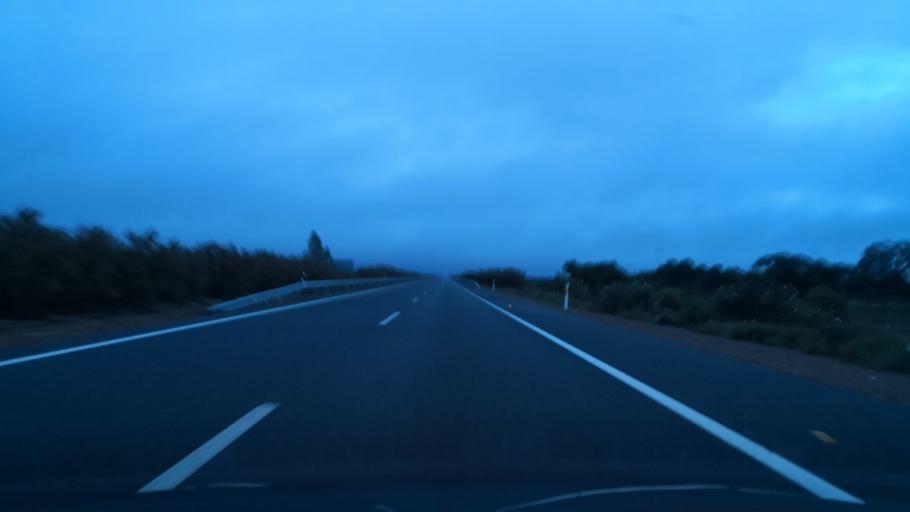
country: ES
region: Extremadura
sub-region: Provincia de Badajoz
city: Aljucen
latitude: 39.0889
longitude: -6.2925
